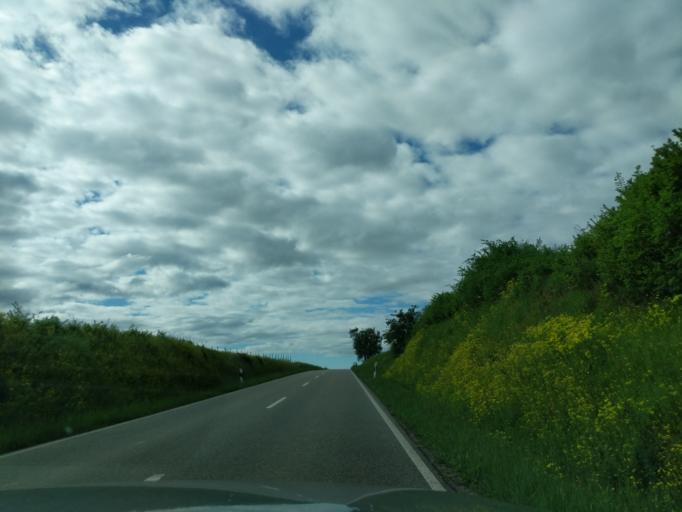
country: DE
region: Rheinland-Pfalz
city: Laumersheim
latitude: 49.5367
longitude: 8.2397
